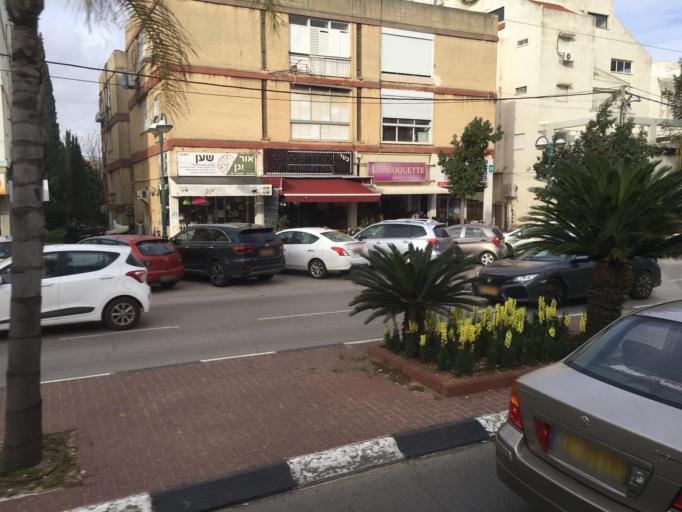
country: IL
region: Central District
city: Kfar Saba
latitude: 32.1774
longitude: 34.8995
